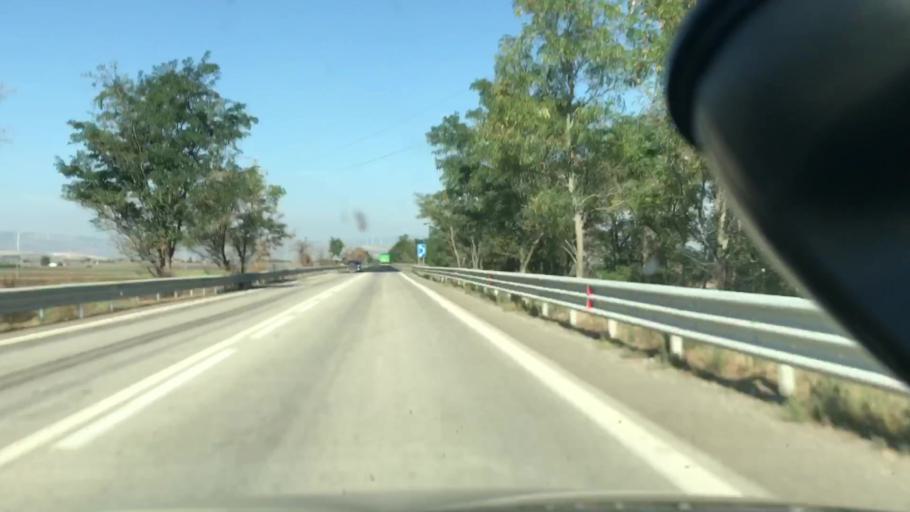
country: IT
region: Basilicate
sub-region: Provincia di Potenza
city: Zona 179
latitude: 41.0763
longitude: 15.6404
